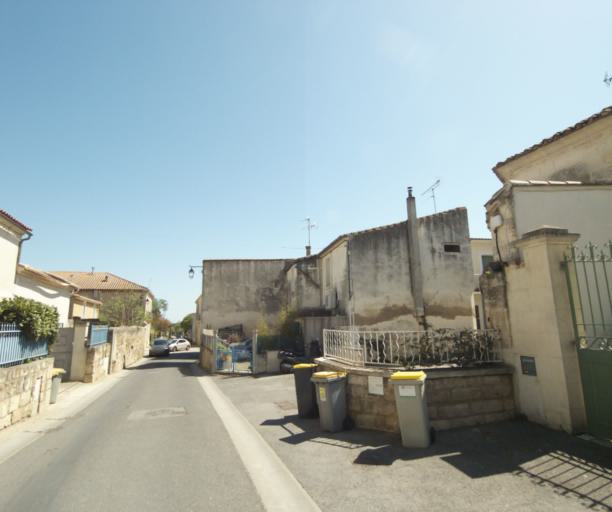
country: FR
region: Languedoc-Roussillon
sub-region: Departement de l'Herault
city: Beaulieu
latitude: 43.7283
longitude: 4.0223
